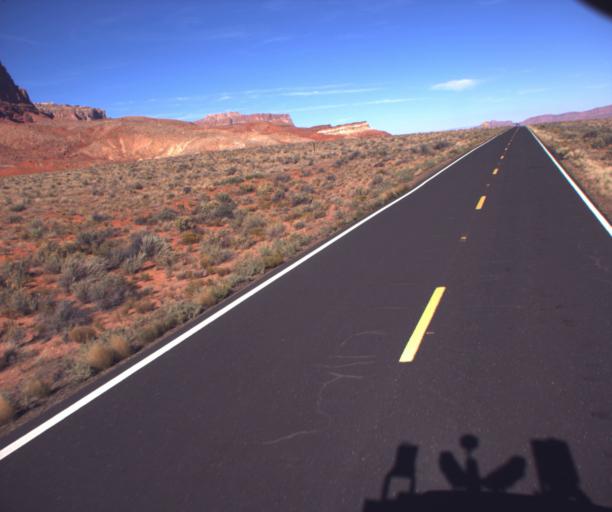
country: US
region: Arizona
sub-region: Coconino County
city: LeChee
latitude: 36.6938
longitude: -111.8130
